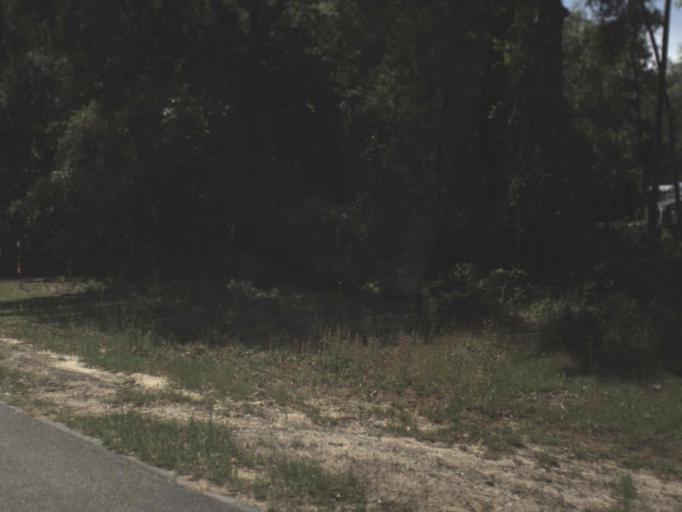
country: US
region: Florida
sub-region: Jackson County
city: Marianna
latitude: 30.6450
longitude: -85.2027
